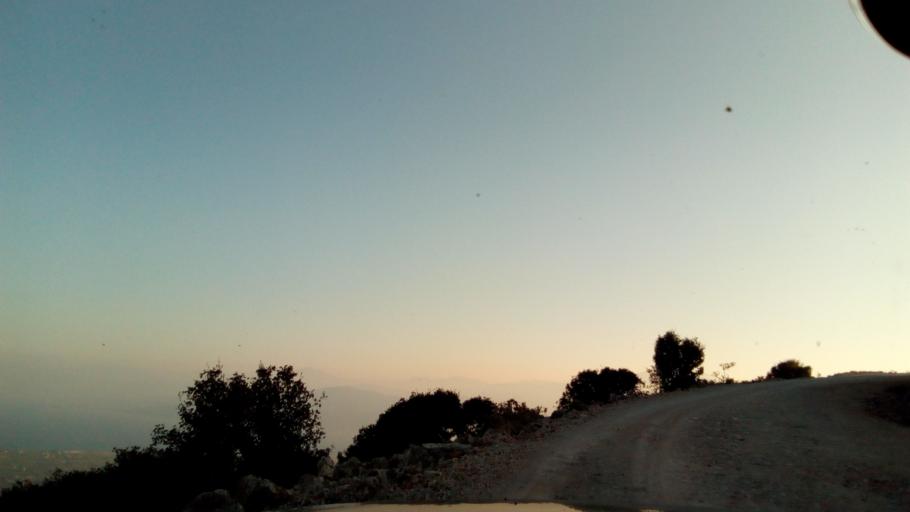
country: GR
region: West Greece
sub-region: Nomos Aitolias kai Akarnanias
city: Nafpaktos
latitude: 38.4318
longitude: 21.8571
